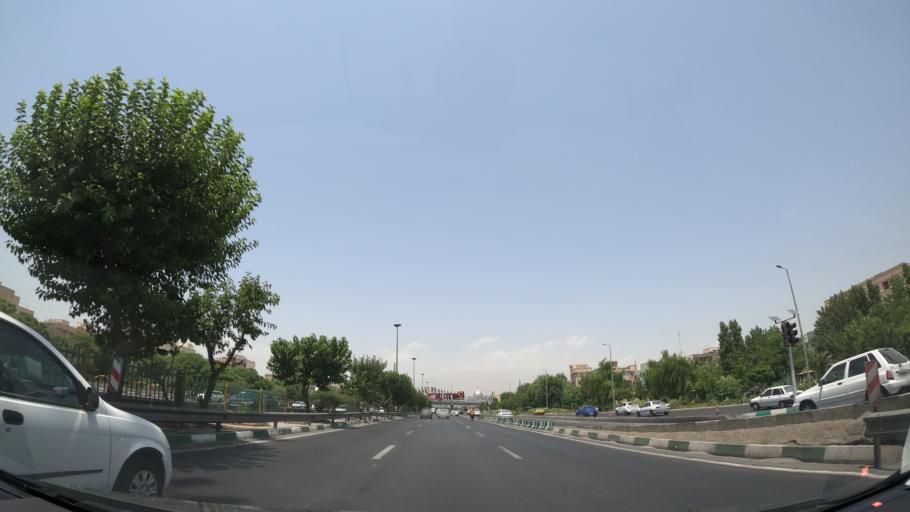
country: IR
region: Tehran
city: Tehran
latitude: 35.6660
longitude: 51.3819
